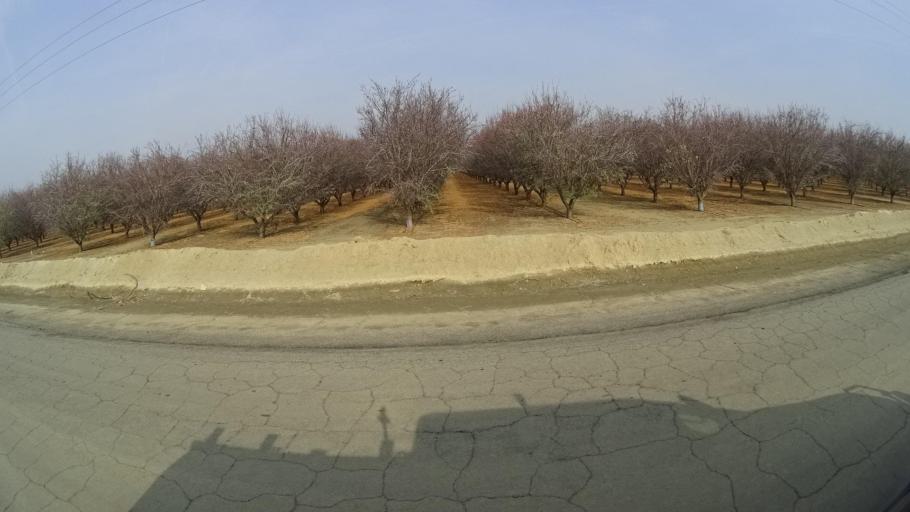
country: US
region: California
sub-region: Kern County
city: Greenfield
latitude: 35.0765
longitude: -119.0421
